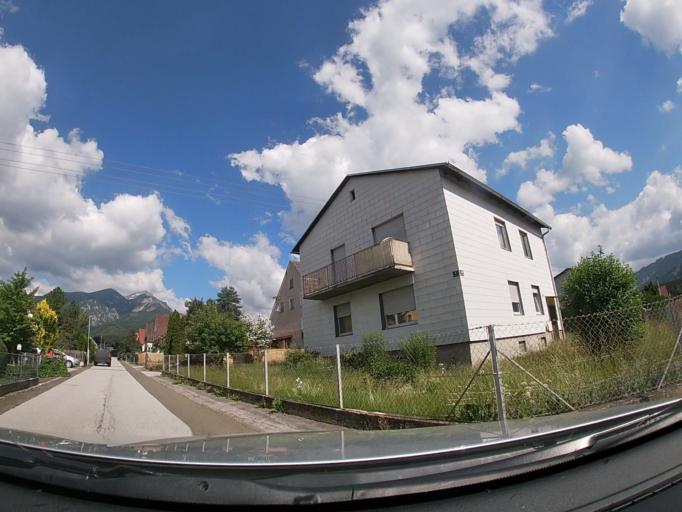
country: AT
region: Styria
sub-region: Politischer Bezirk Leoben
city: Trofaiach
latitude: 47.4236
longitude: 14.9899
